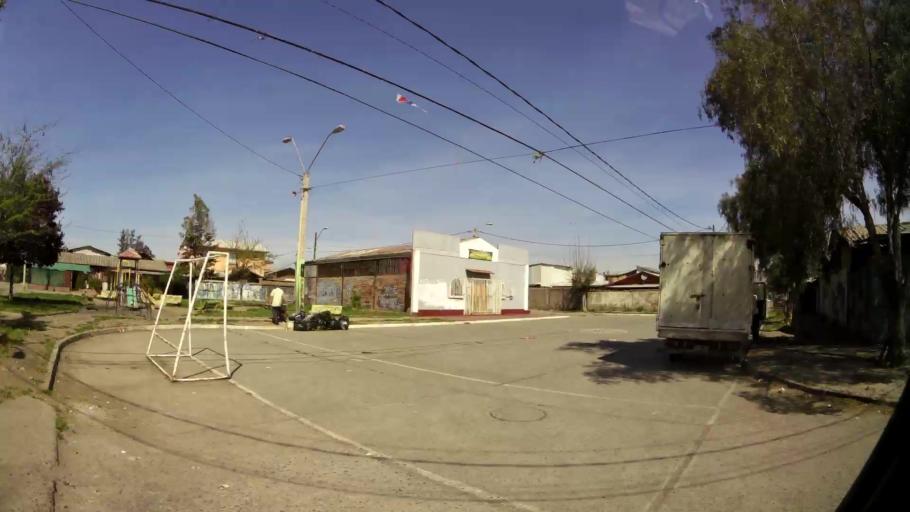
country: CL
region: Santiago Metropolitan
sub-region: Provincia de Maipo
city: San Bernardo
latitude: -33.5281
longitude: -70.6994
